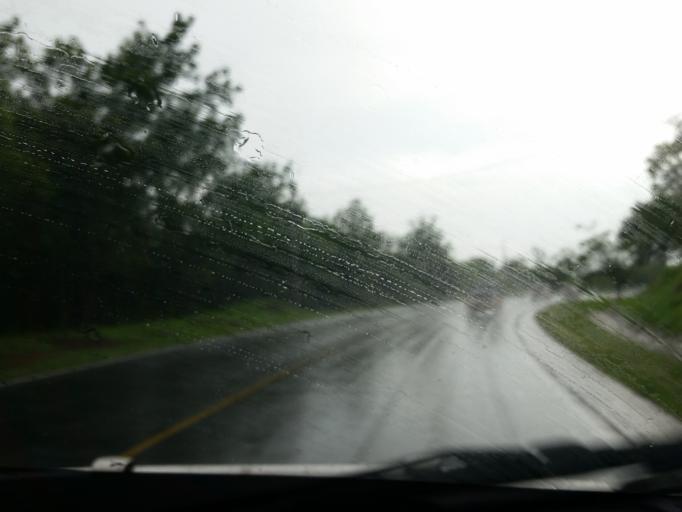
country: NI
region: Matagalpa
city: Ciudad Dario
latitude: 12.6221
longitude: -86.0481
